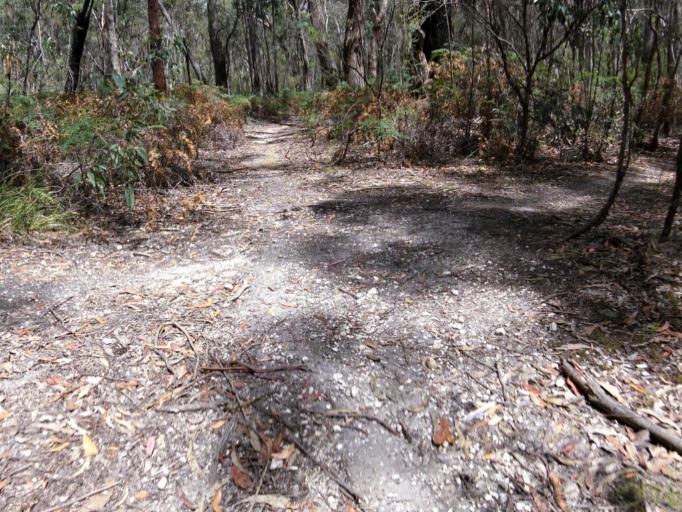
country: AU
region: Victoria
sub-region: Melton
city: Melton West
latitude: -37.4852
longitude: 144.5386
